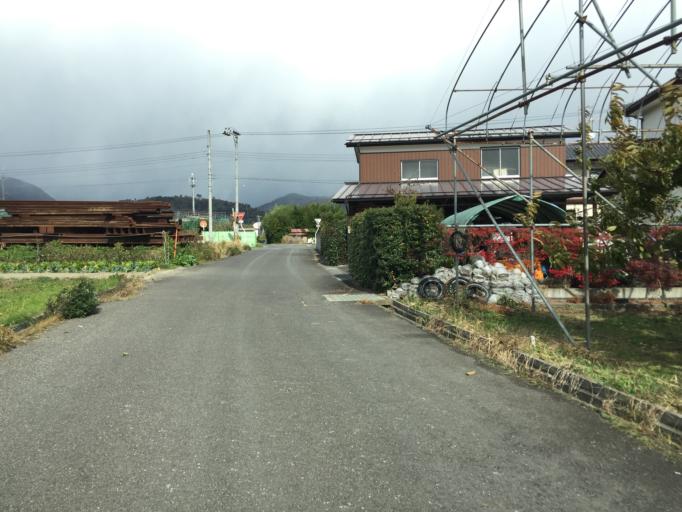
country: JP
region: Fukushima
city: Fukushima-shi
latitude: 37.8163
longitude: 140.4387
